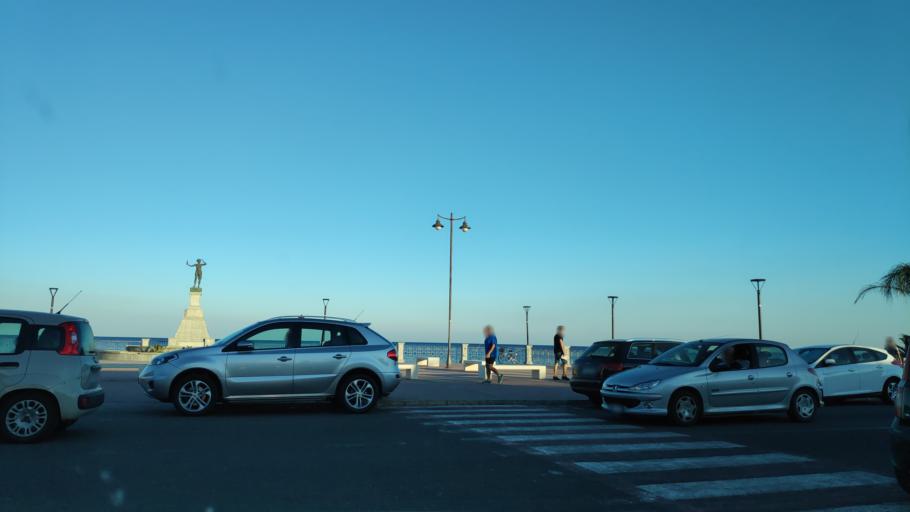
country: IT
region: Calabria
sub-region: Provincia di Reggio Calabria
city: Locri
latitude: 38.2347
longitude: 16.2674
